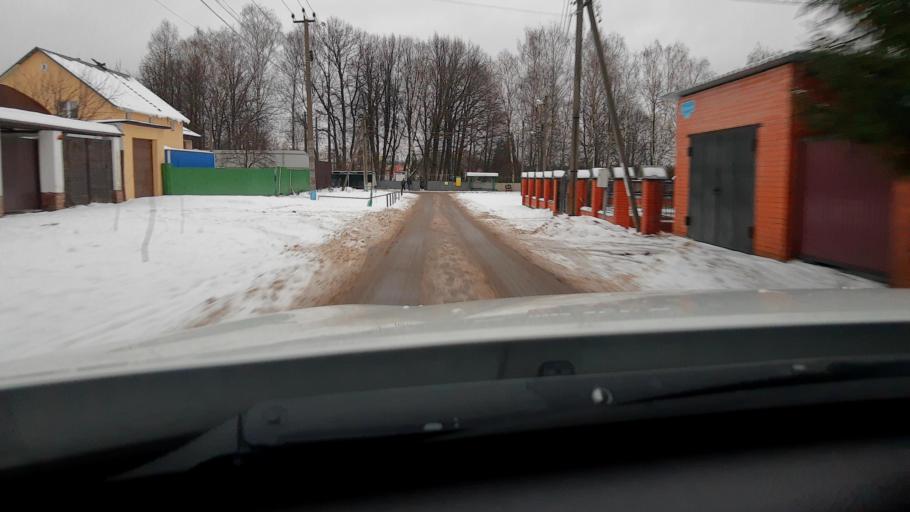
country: RU
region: Moskovskaya
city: Krasnogorsk
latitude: 55.8637
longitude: 37.3137
